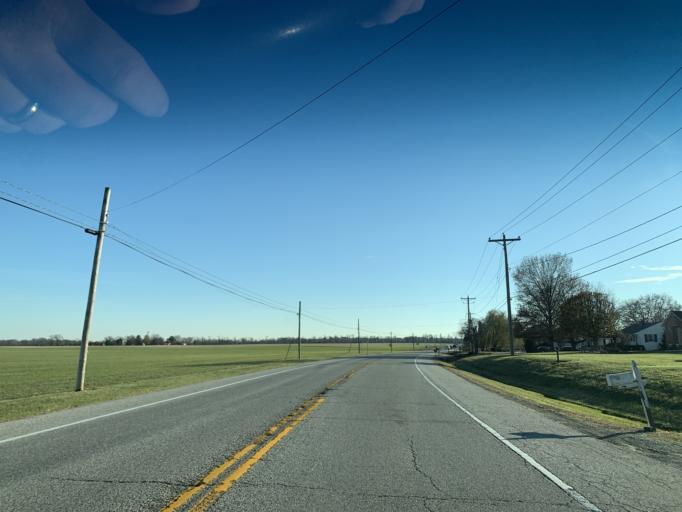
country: US
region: Delaware
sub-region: New Castle County
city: Middletown
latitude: 39.3965
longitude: -75.8710
